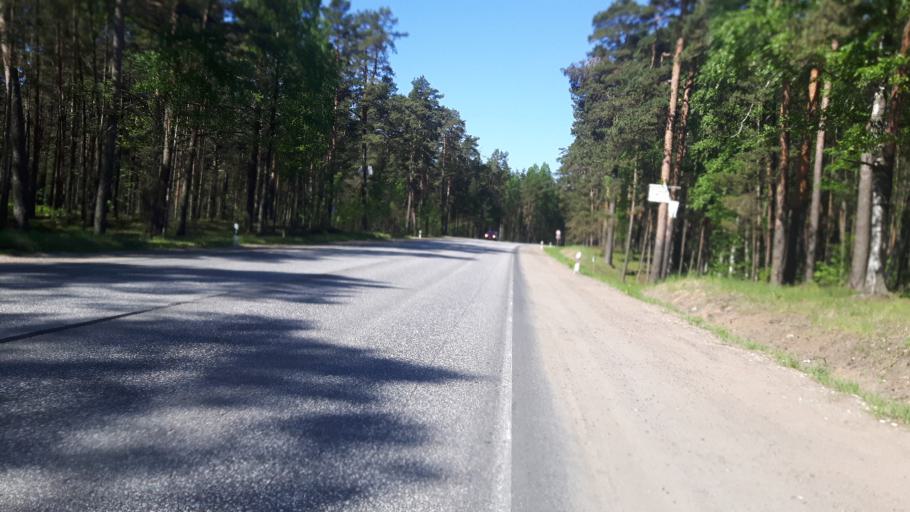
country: RU
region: Leningrad
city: Lebyazh'ye
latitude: 59.9570
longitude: 29.4603
